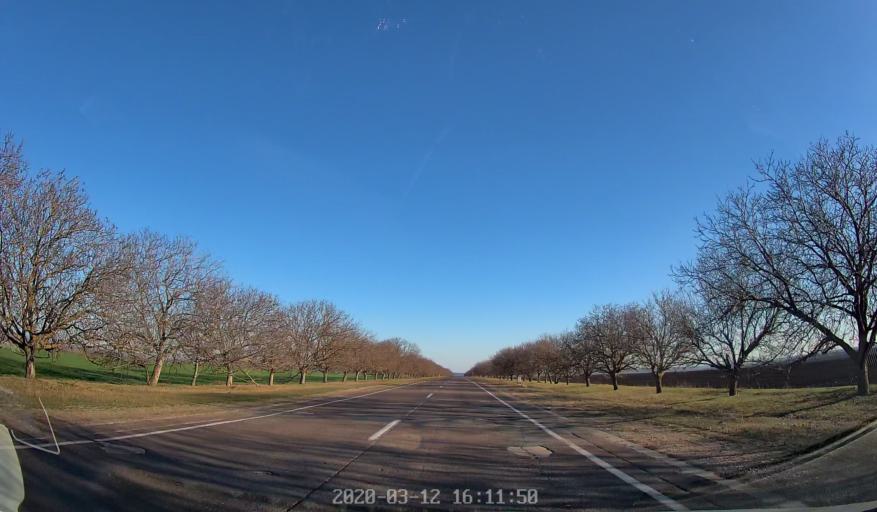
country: MD
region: Anenii Noi
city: Anenii Noi
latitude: 46.9432
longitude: 29.2646
